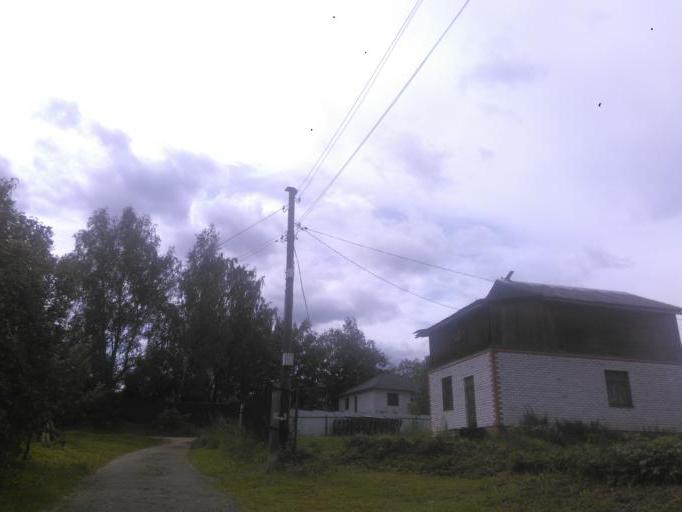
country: RU
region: Moskovskaya
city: Solnechnogorsk
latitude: 56.1507
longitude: 36.9165
